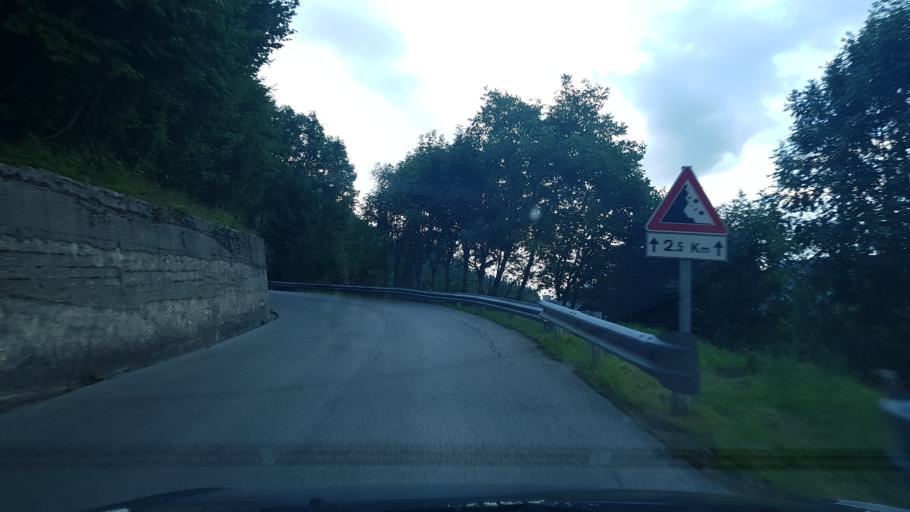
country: IT
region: Friuli Venezia Giulia
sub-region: Provincia di Udine
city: Forni Avoltri
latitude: 46.5869
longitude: 12.7776
